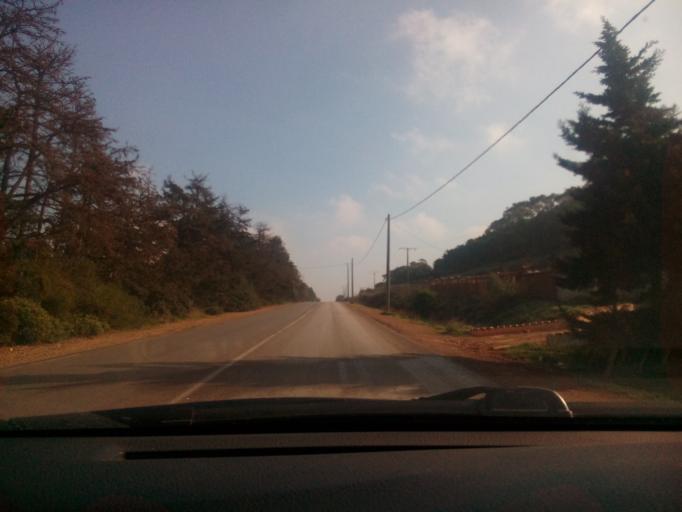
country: DZ
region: Oran
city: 'Ain el Turk
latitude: 35.7040
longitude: -0.8353
